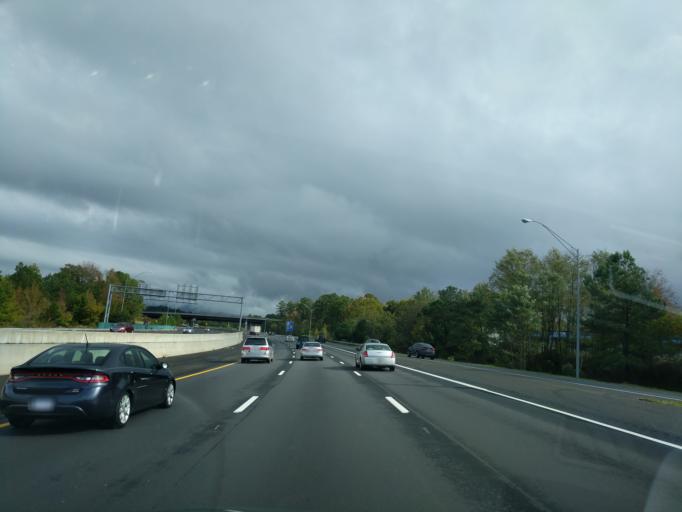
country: US
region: North Carolina
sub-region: Durham County
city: Durham
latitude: 36.0252
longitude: -78.9532
